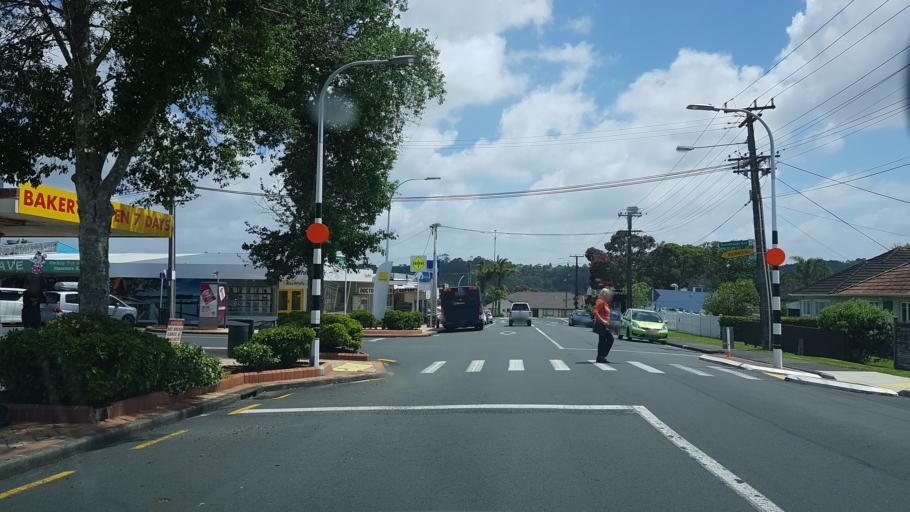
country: NZ
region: Auckland
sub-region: Auckland
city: North Shore
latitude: -36.7926
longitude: 174.6877
